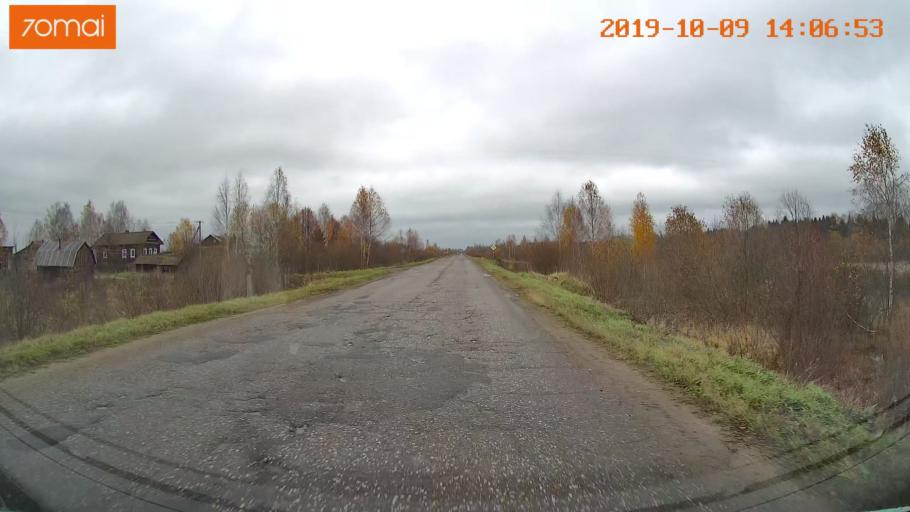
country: RU
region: Kostroma
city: Buy
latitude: 58.4671
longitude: 41.4156
